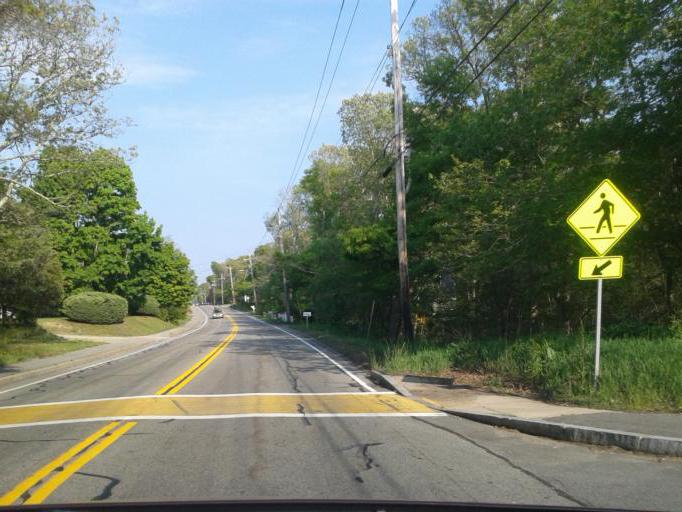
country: US
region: Massachusetts
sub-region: Barnstable County
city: Teaticket
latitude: 41.5833
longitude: -70.5999
